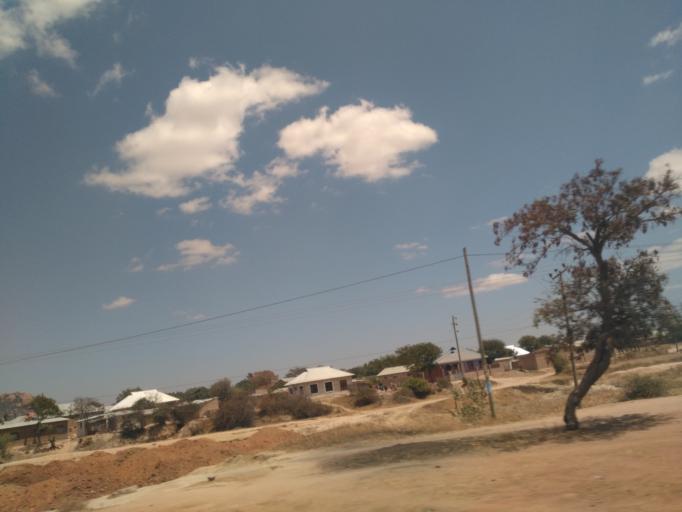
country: TZ
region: Dodoma
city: Kisasa
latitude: -6.1653
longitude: 35.7859
